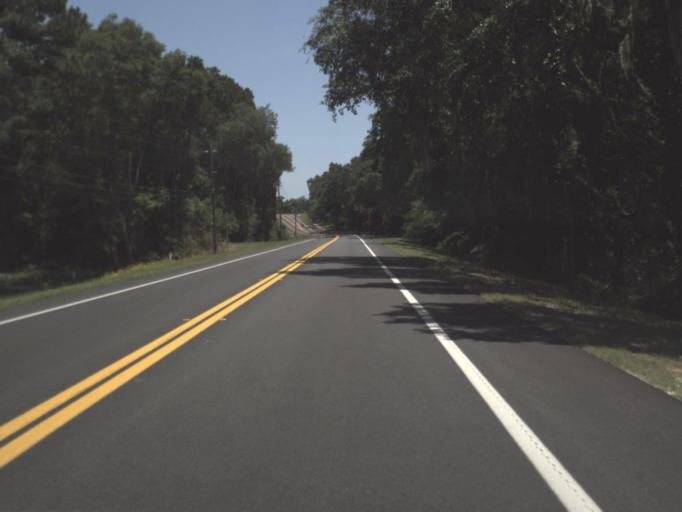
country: US
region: Florida
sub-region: Suwannee County
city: Wellborn
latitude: 30.1920
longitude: -82.7414
